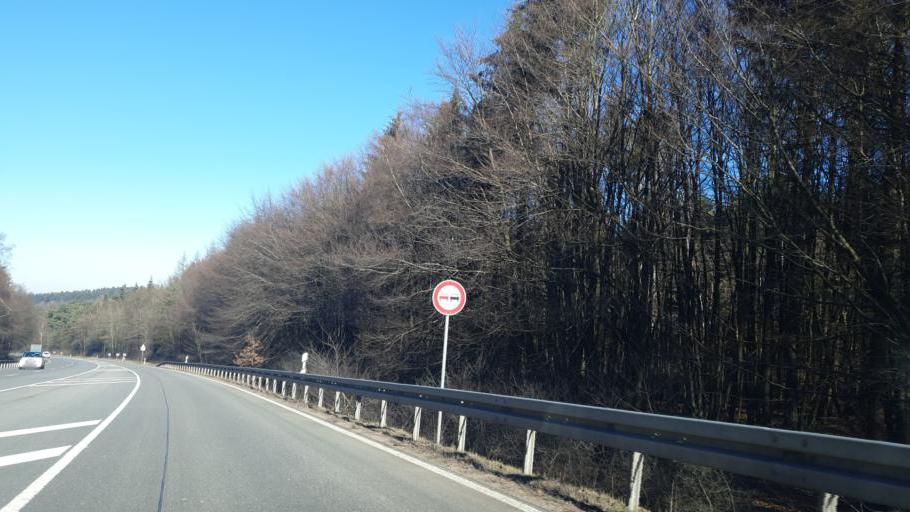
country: DE
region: Hesse
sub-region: Regierungsbezirk Darmstadt
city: Wiesbaden
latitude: 50.1375
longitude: 8.2190
